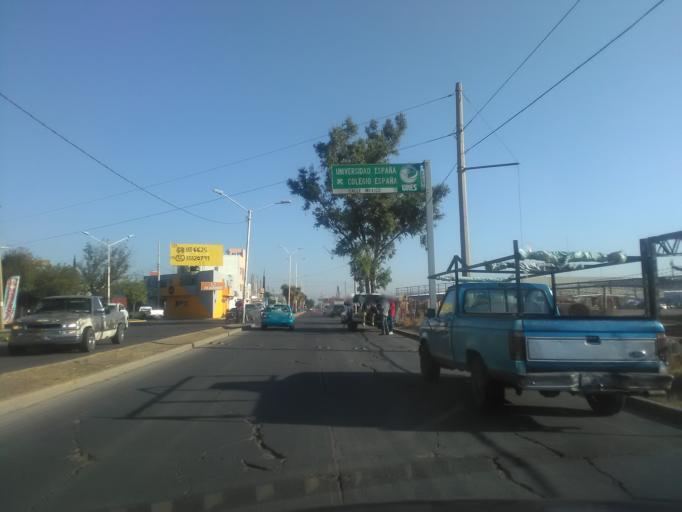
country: MX
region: Durango
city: Victoria de Durango
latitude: 24.0441
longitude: -104.6223
